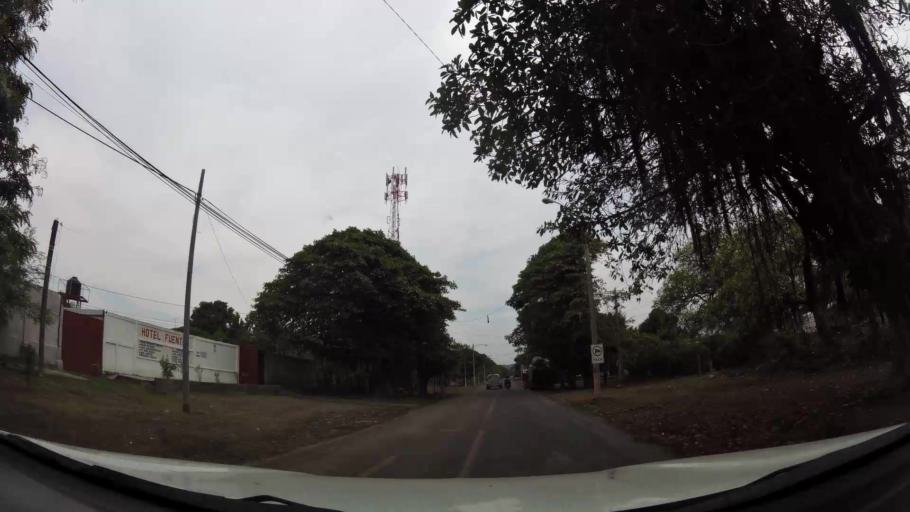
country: NI
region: Granada
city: Granada
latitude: 11.9197
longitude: -85.9664
